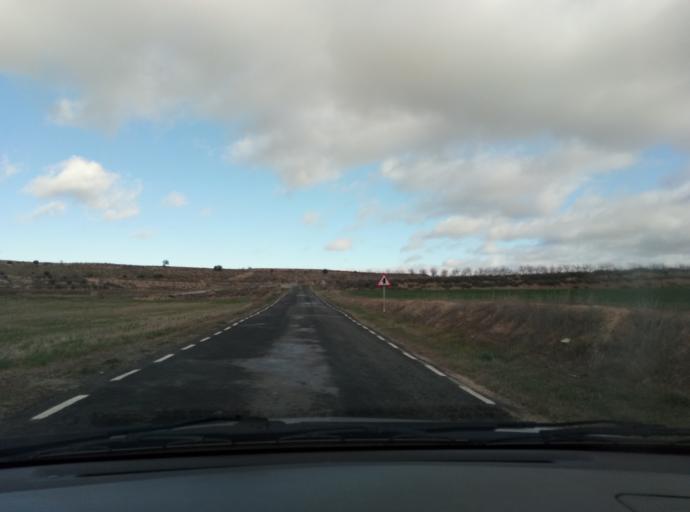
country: ES
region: Catalonia
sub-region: Provincia de Lleida
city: Verdu
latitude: 41.6069
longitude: 1.1044
